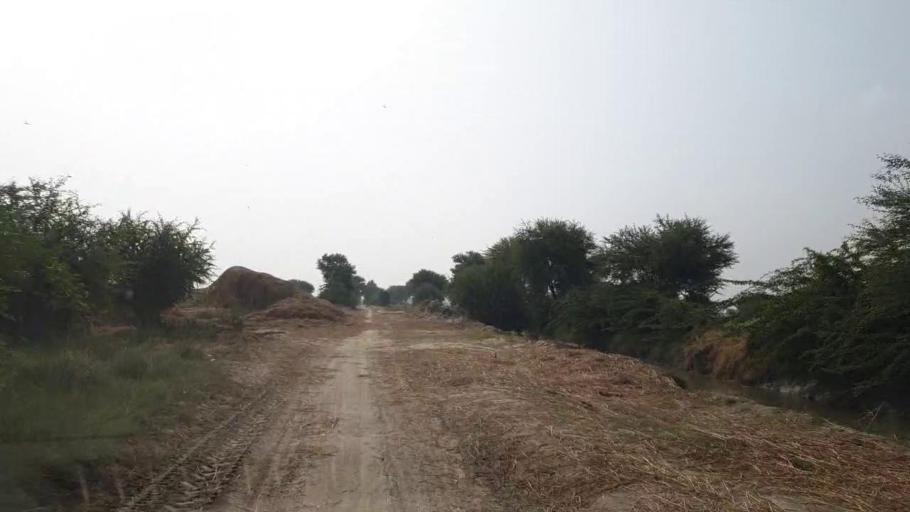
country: PK
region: Sindh
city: Kario
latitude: 24.7681
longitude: 68.5637
